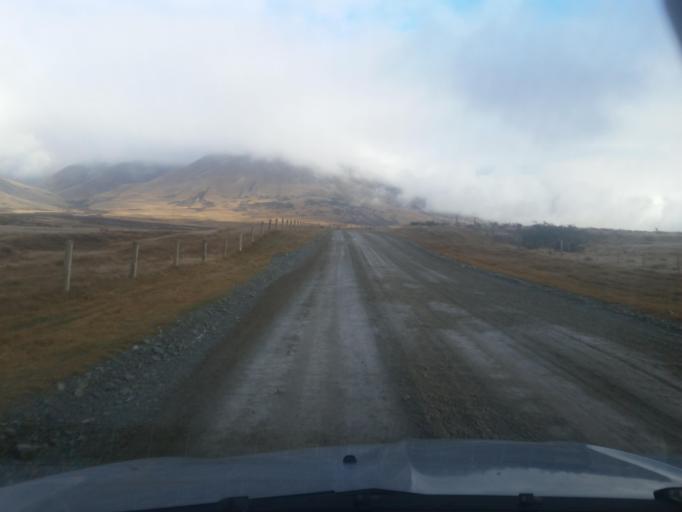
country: NZ
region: Canterbury
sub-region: Ashburton District
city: Methven
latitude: -43.6165
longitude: 171.0864
